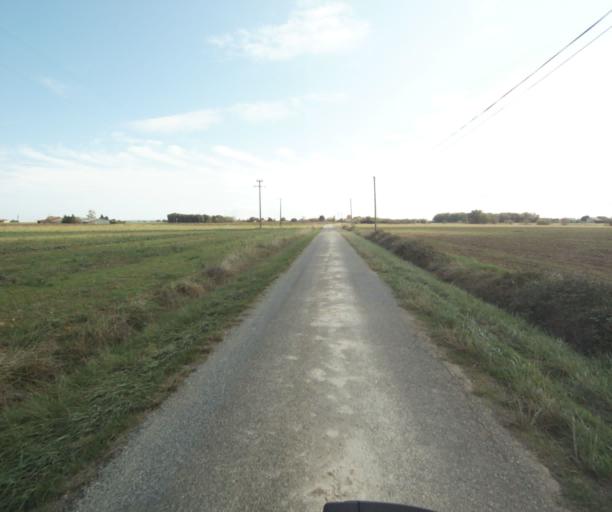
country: FR
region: Midi-Pyrenees
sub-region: Departement du Tarn-et-Garonne
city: Verdun-sur-Garonne
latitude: 43.8459
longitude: 1.1723
